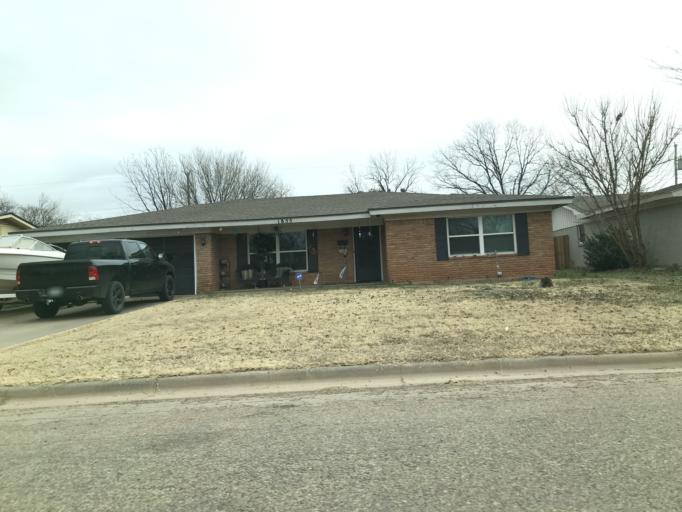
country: US
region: Texas
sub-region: Taylor County
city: Abilene
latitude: 32.4714
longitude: -99.7621
